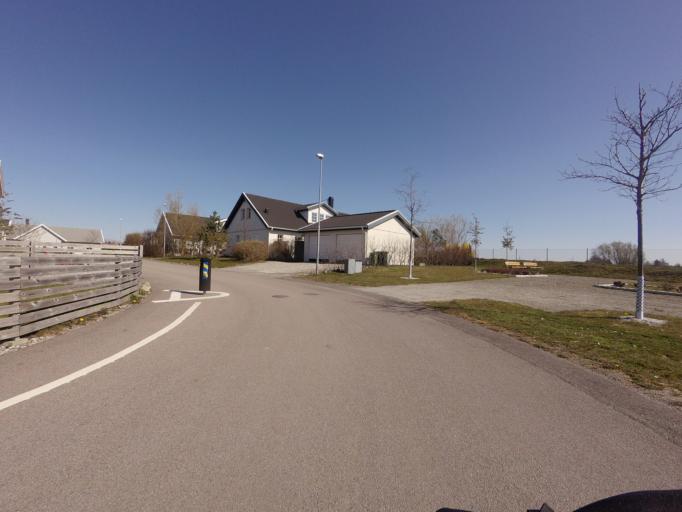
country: SE
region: Skane
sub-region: Malmo
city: Oxie
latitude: 55.4626
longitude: 13.1396
